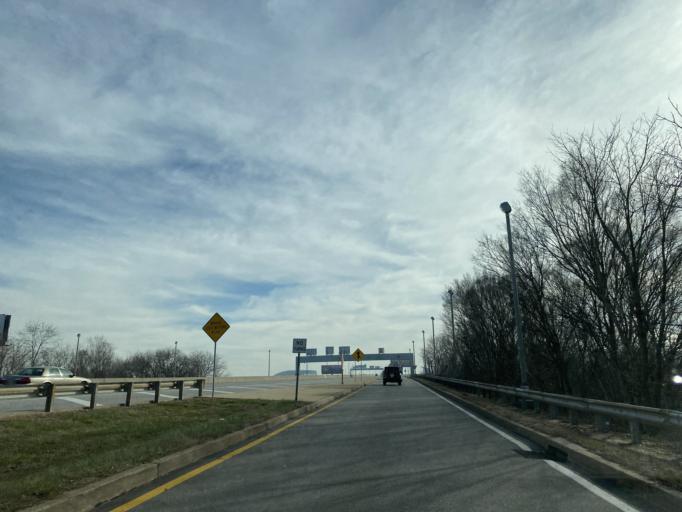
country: US
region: New Jersey
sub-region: Camden County
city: Pennsauken
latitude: 39.9921
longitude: -75.0782
